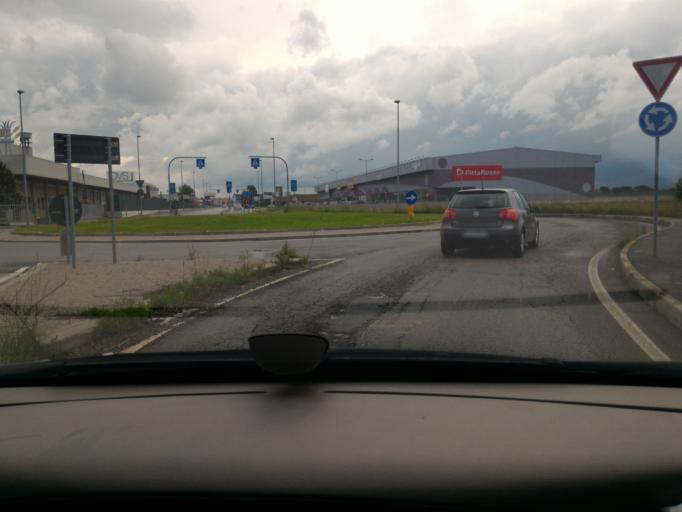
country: IT
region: Piedmont
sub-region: Provincia di Cuneo
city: Genola
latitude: 44.6020
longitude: 7.6604
